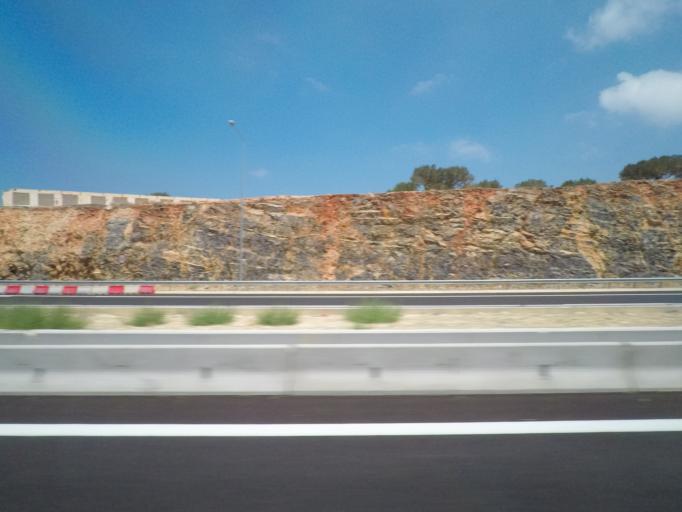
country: GR
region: Crete
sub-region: Nomos Irakleiou
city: Gournes
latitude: 35.3239
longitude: 25.2963
